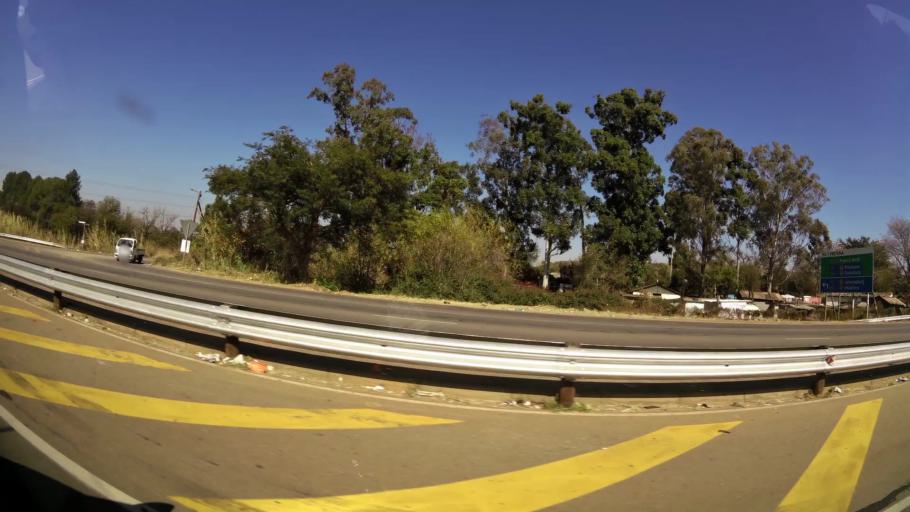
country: ZA
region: Gauteng
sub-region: City of Tshwane Metropolitan Municipality
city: Pretoria
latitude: -25.6851
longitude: 28.2849
